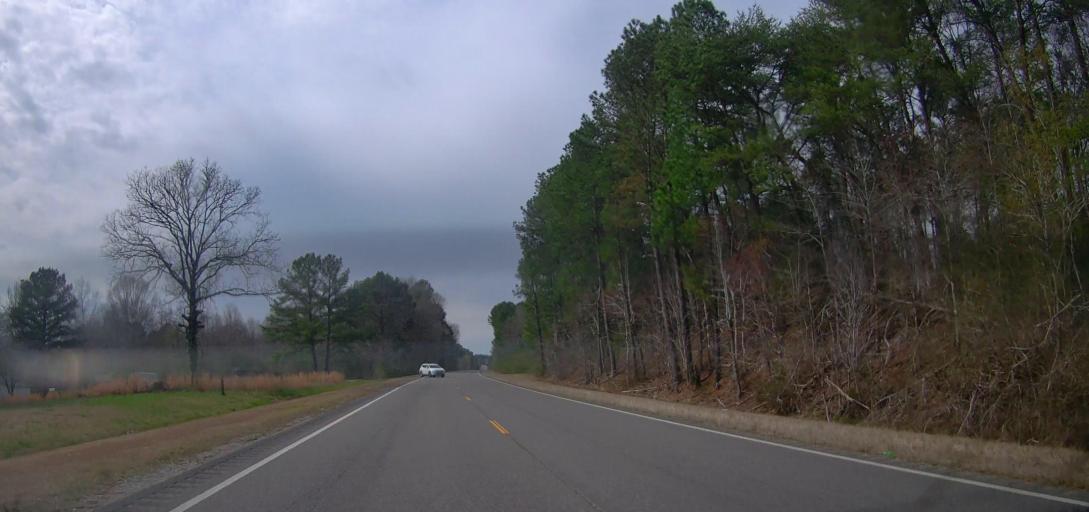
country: US
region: Alabama
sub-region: Walker County
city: Carbon Hill
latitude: 33.9025
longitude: -87.5478
